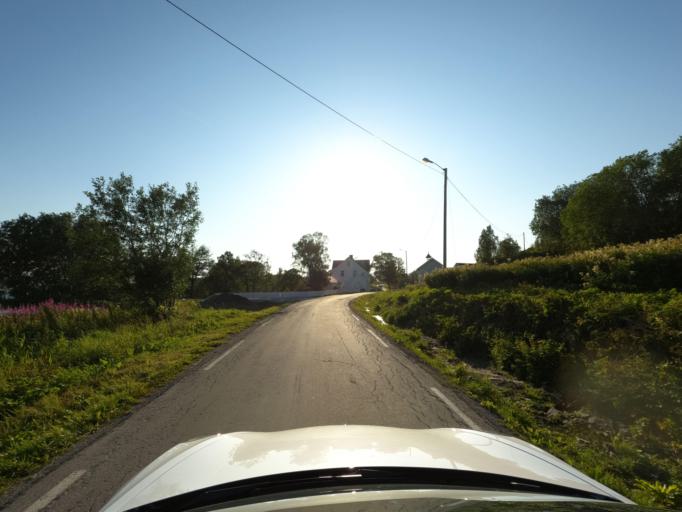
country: NO
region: Nordland
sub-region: Ballangen
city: Ballangen
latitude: 68.4583
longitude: 16.7017
